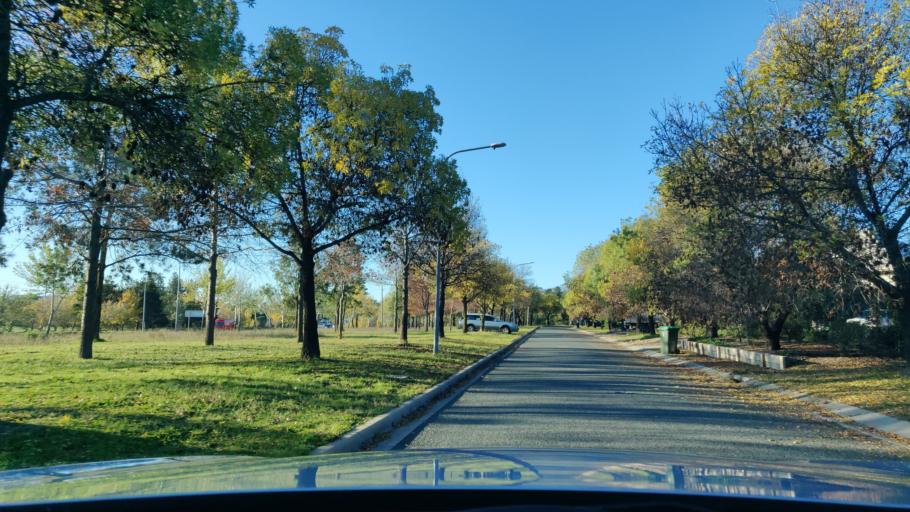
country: AU
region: Australian Capital Territory
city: Macarthur
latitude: -35.4408
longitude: 149.1228
